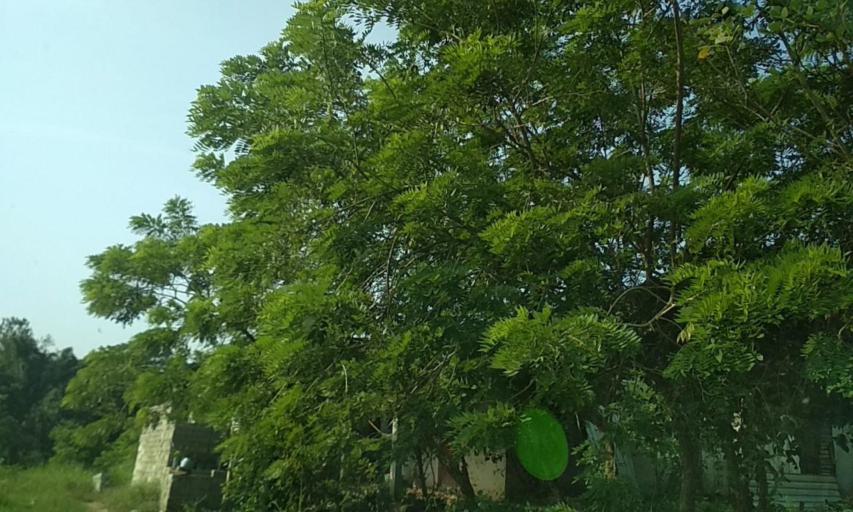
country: MX
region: Veracruz
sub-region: Martinez de la Torre
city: El Progreso
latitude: 20.1492
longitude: -97.0675
